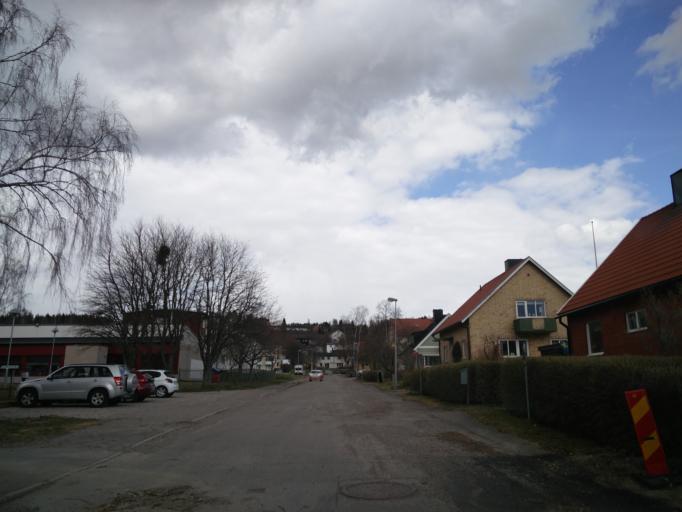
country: SE
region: Vaesternorrland
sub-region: Sundsvalls Kommun
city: Sundsvall
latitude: 62.4036
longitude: 17.2580
